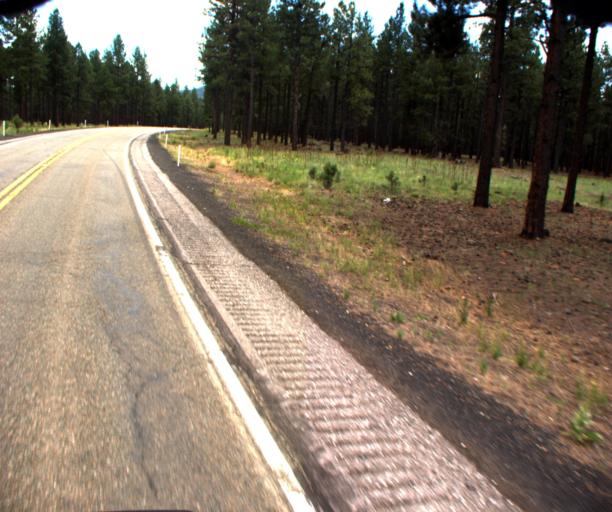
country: US
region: Arizona
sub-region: Coconino County
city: Flagstaff
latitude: 35.2789
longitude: -111.7459
